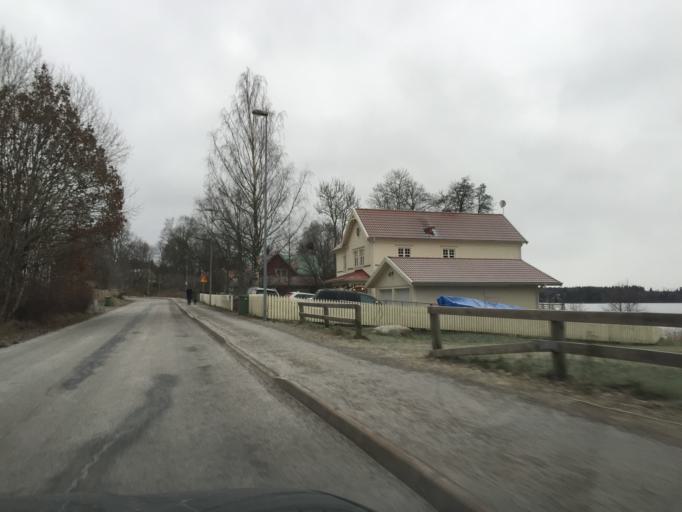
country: SE
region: Stockholm
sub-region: Salems Kommun
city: Ronninge
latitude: 59.1839
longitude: 17.7236
